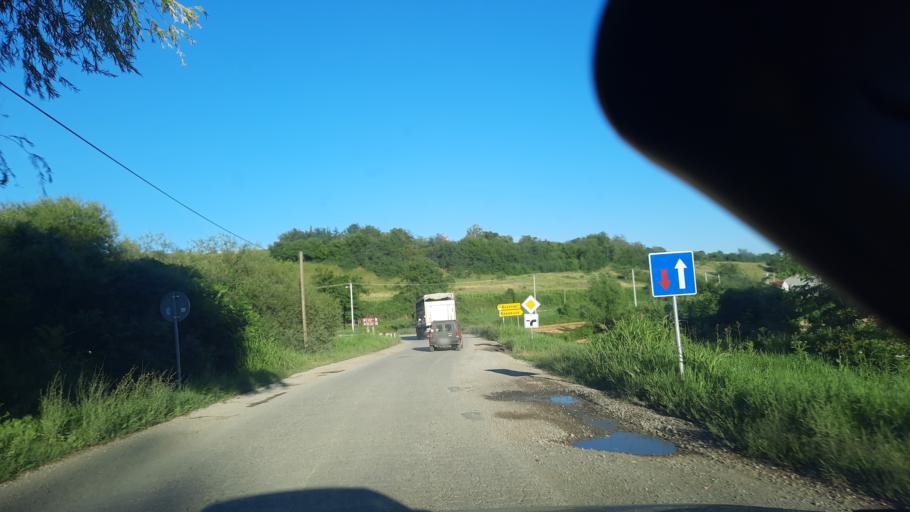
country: RS
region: Autonomna Pokrajina Vojvodina
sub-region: Juznobacki Okrug
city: Sremski Karlovci
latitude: 45.1224
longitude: 19.9424
